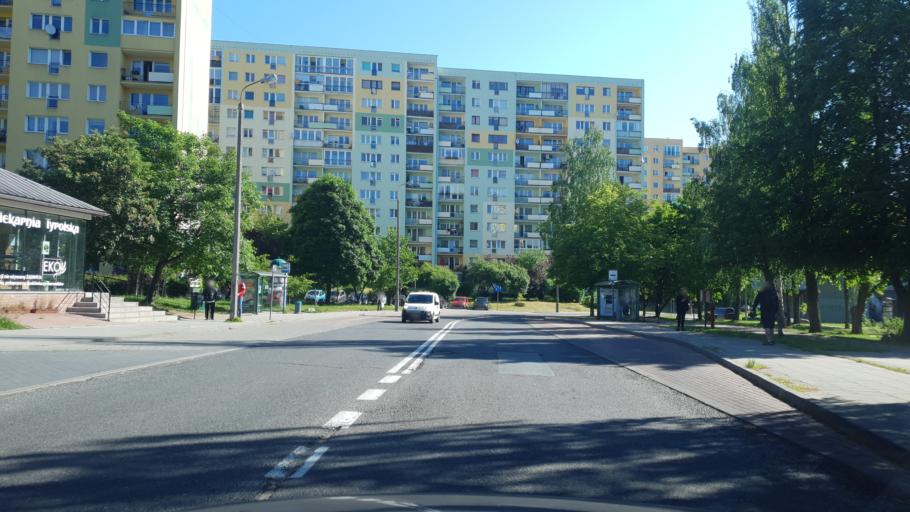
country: PL
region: Pomeranian Voivodeship
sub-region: Sopot
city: Sopot
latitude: 54.4574
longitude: 18.5339
